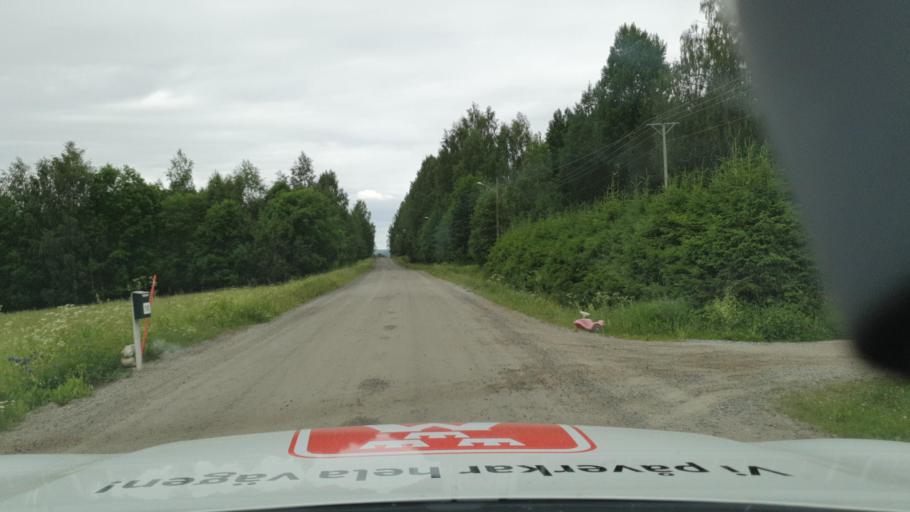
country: SE
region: Vaesterbotten
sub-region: Bjurholms Kommun
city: Bjurholm
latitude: 63.7790
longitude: 19.3916
